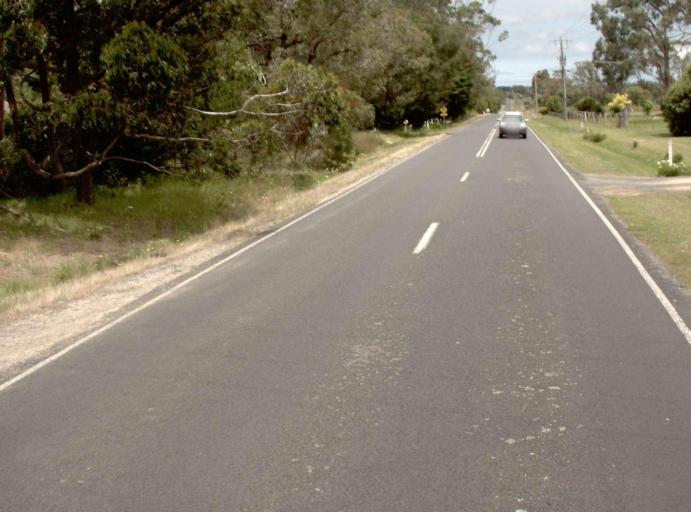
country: AU
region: Victoria
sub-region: Latrobe
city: Traralgon
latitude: -38.5393
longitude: 146.6569
